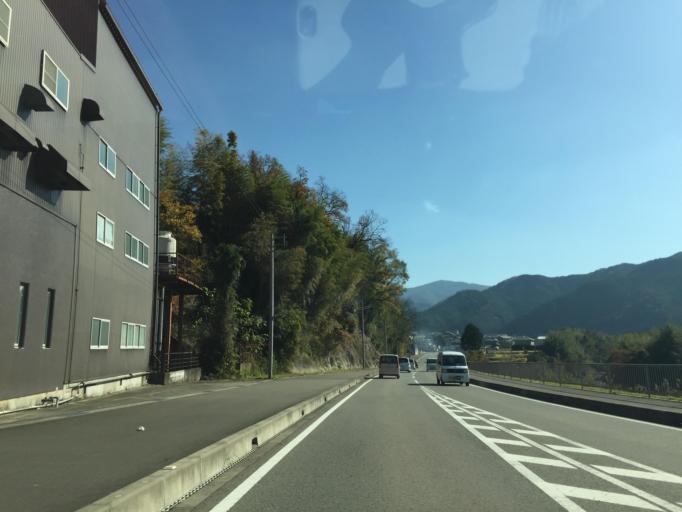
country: JP
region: Wakayama
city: Iwade
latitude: 34.1623
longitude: 135.3081
